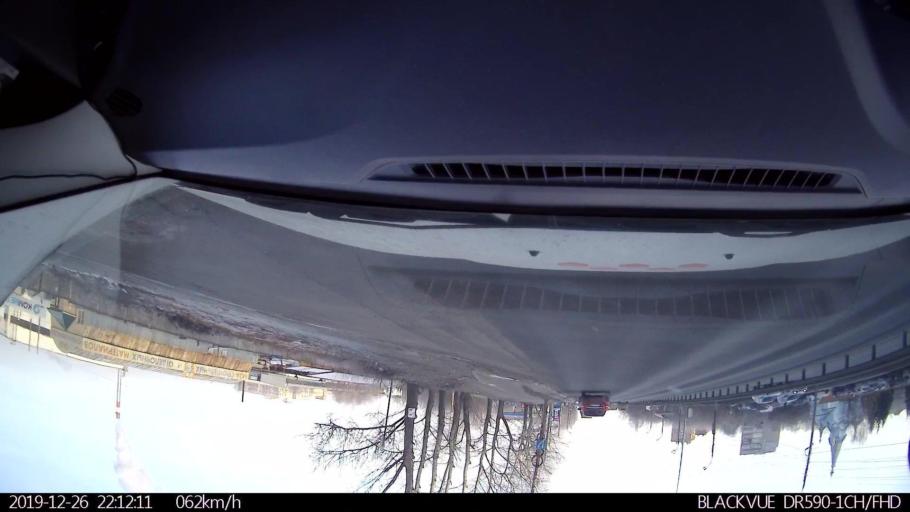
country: RU
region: Nizjnij Novgorod
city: Nizhniy Novgorod
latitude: 56.2418
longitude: 43.9752
